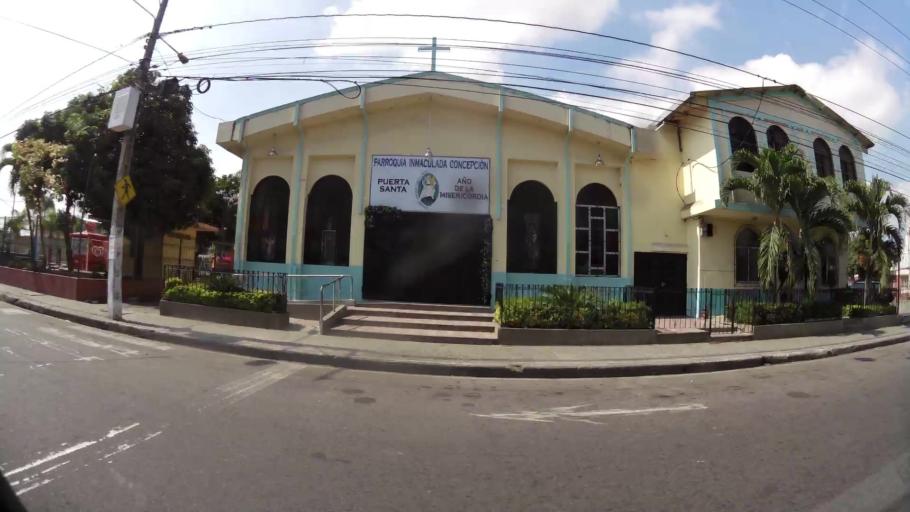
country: EC
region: Guayas
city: Eloy Alfaro
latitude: -2.1630
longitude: -79.8430
